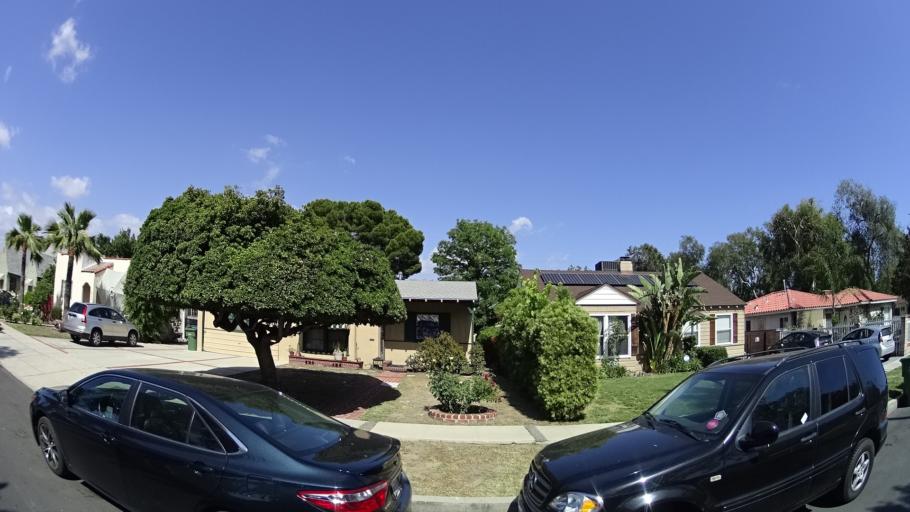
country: US
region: California
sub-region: Los Angeles County
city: North Hollywood
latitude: 34.1779
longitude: -118.3867
